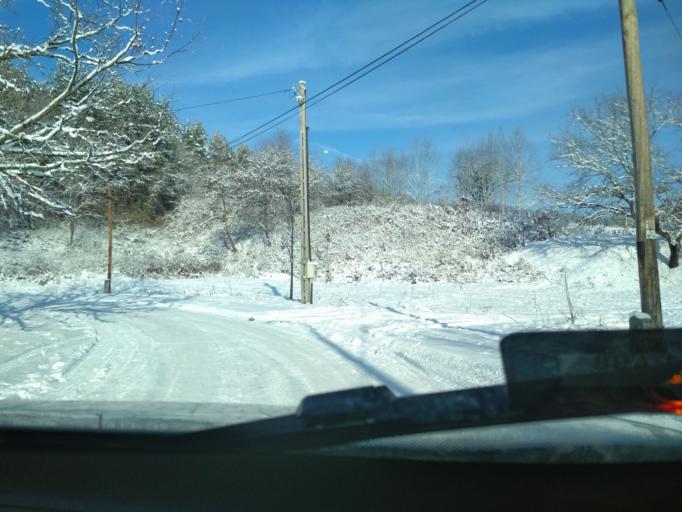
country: HU
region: Nograd
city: Somoskoujfalu
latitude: 48.1326
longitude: 19.8232
